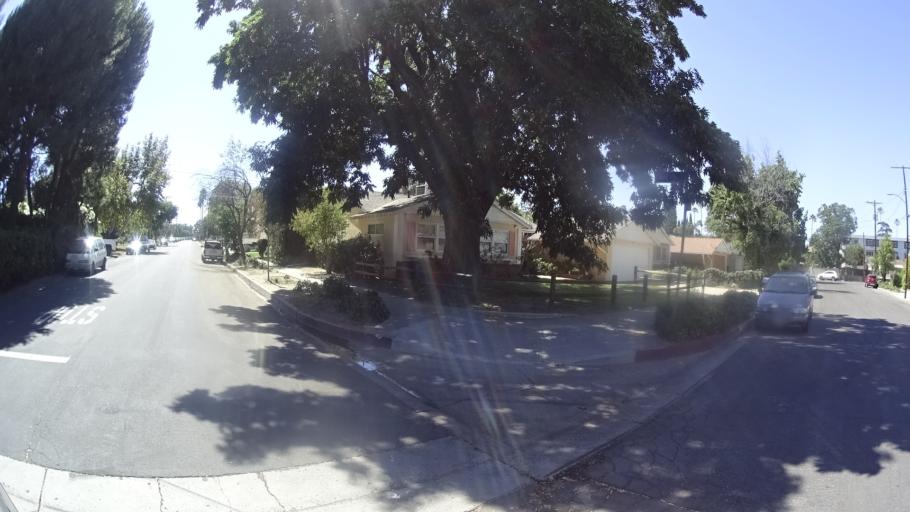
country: US
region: California
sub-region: Los Angeles County
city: Van Nuys
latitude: 34.1994
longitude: -118.4794
